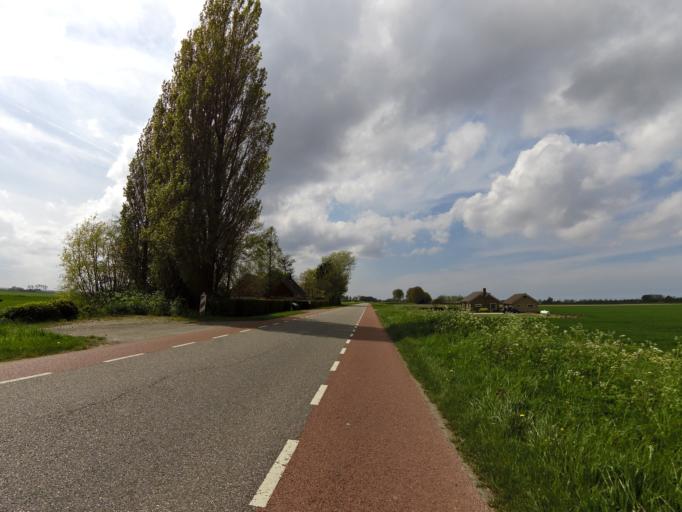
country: NL
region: South Holland
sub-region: Gemeente Hellevoetsluis
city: Nieuwenhoorn
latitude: 51.8272
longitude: 4.2300
